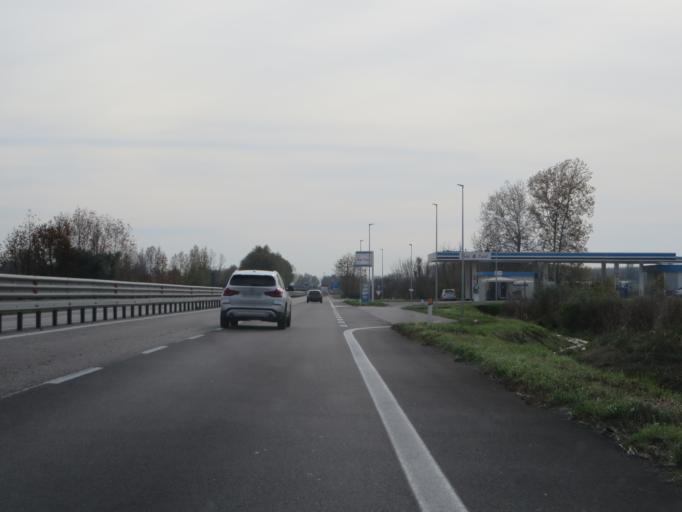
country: IT
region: Veneto
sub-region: Provincia di Verona
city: San Pietro di Morubio
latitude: 45.2393
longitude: 11.2365
